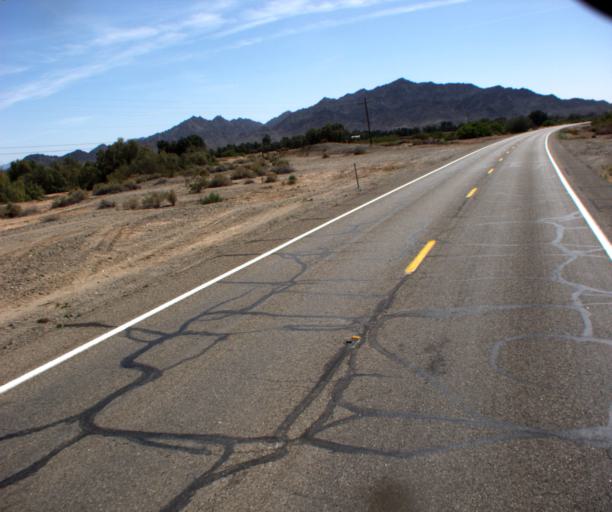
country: US
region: Arizona
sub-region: Yuma County
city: Fortuna Foothills
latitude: 32.7821
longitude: -114.3823
